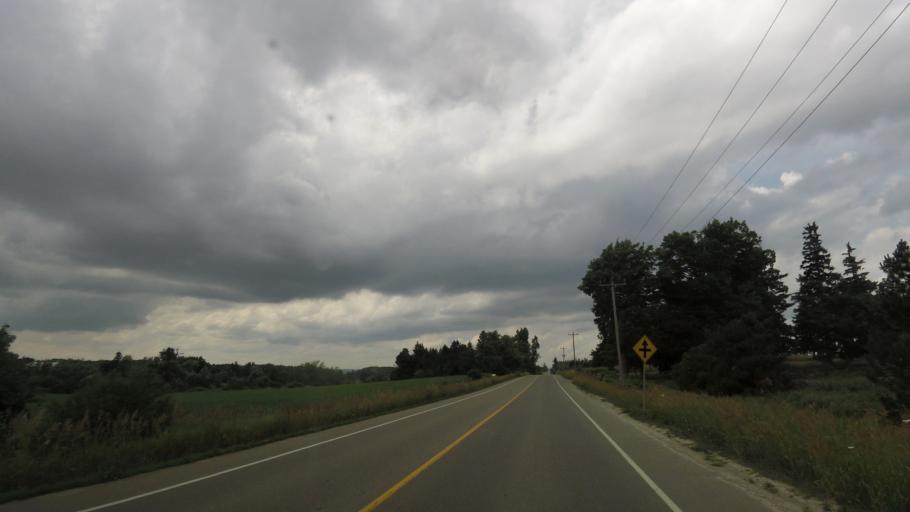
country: CA
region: Ontario
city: Brampton
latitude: 43.7611
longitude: -79.8382
